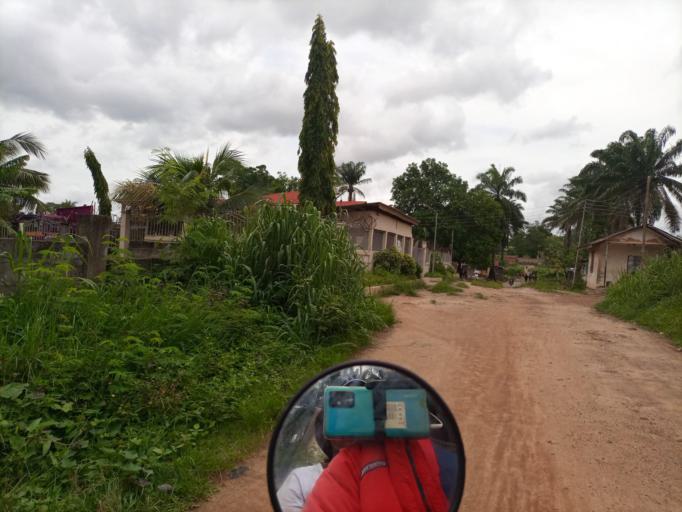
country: SL
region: Southern Province
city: Bo
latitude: 7.9500
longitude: -11.7448
